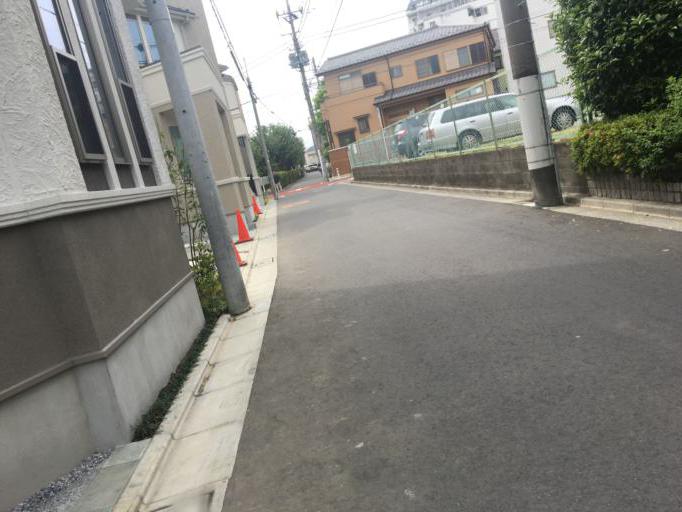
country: JP
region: Saitama
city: Shimotoda
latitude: 35.7637
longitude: 139.6703
